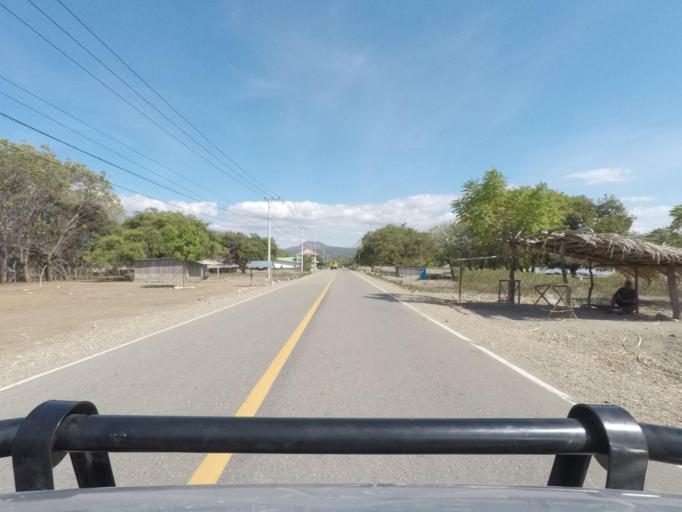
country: ID
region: East Nusa Tenggara
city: Atambua
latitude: -8.9373
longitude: 124.9793
